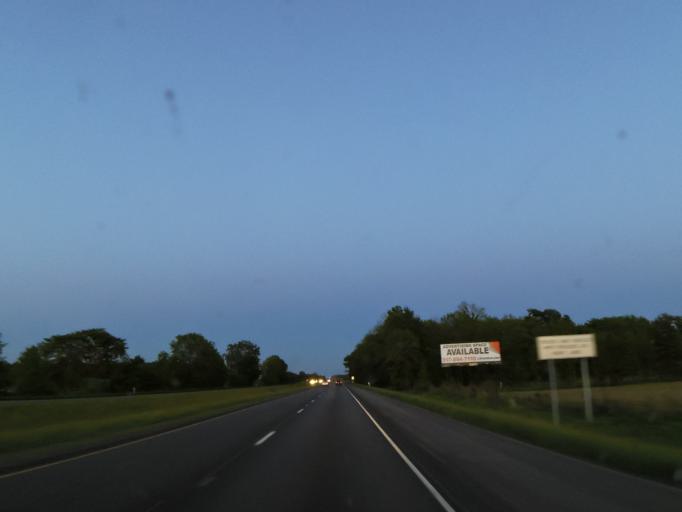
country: US
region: Indiana
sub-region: Hendricks County
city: Pittsboro
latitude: 39.8871
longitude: -86.5262
